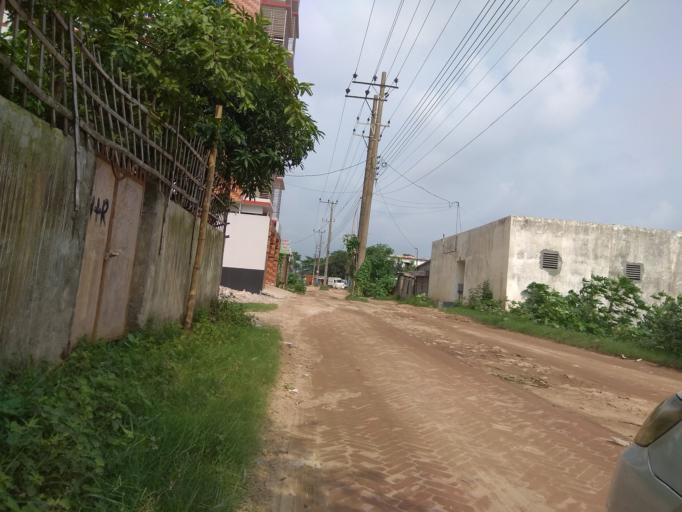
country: BD
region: Dhaka
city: Tungi
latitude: 23.8324
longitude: 90.3502
